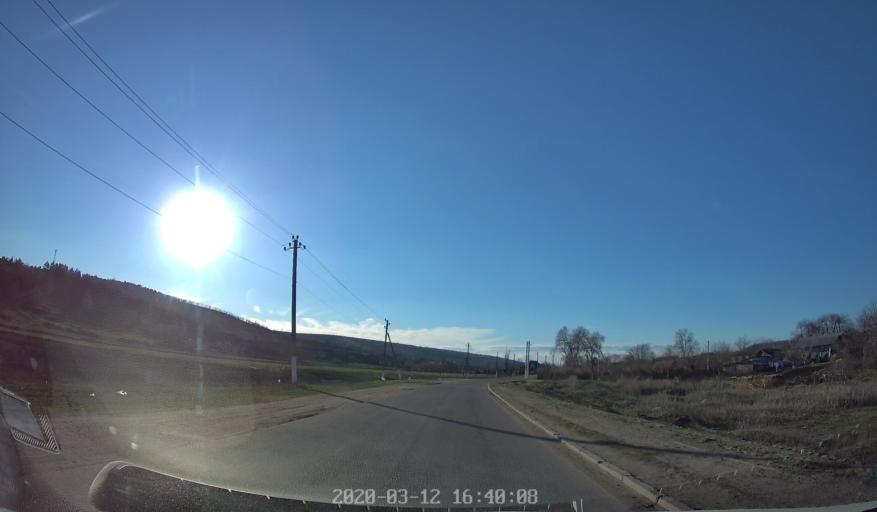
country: MD
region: Anenii Noi
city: Anenii Noi
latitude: 46.8167
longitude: 29.1525
